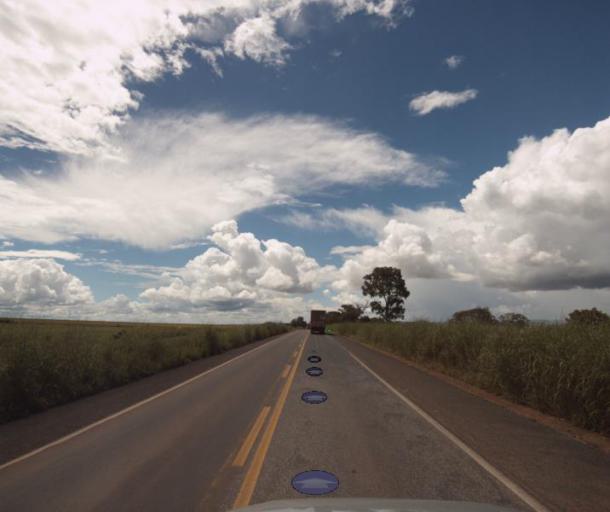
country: BR
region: Goias
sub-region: Uruacu
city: Uruacu
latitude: -14.1201
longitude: -49.1073
